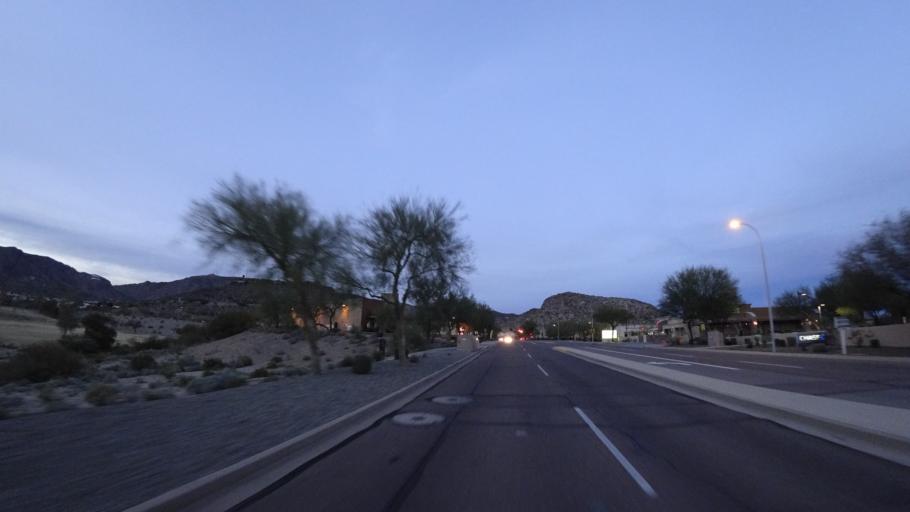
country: US
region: Arizona
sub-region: Maricopa County
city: Guadalupe
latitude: 33.3044
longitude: -112.0568
